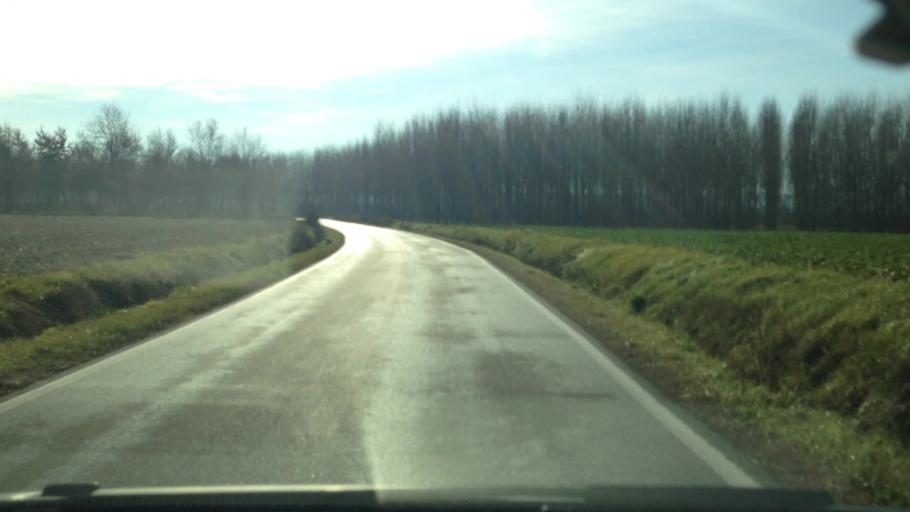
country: IT
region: Piedmont
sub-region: Provincia di Alessandria
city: Quattordio
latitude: 44.8881
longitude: 8.4046
